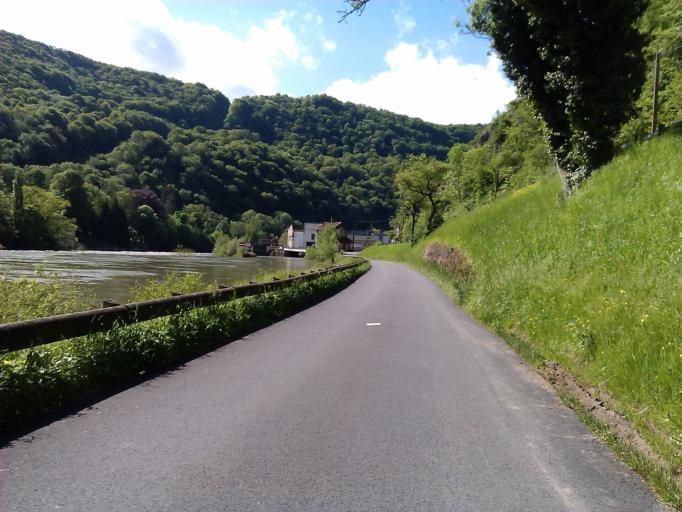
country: FR
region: Franche-Comte
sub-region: Departement du Doubs
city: Roulans
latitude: 47.3029
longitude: 6.2352
